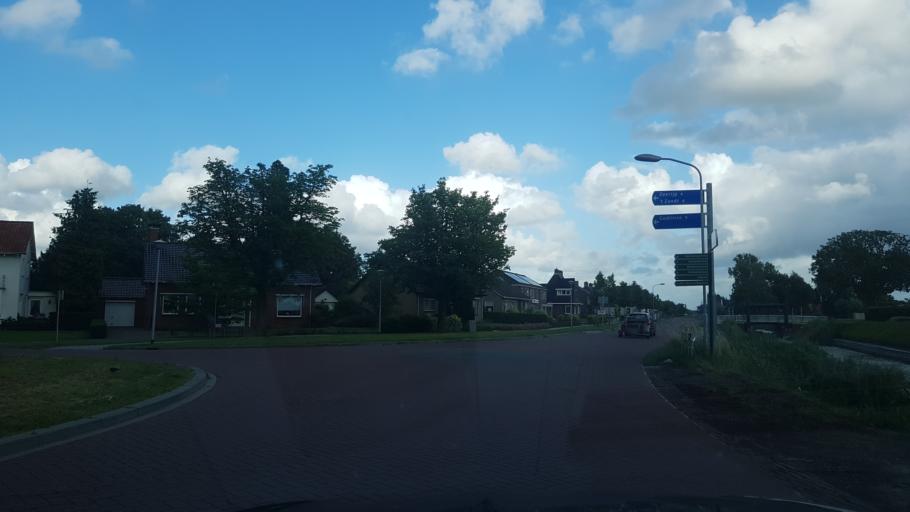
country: NL
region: Groningen
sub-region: Gemeente Appingedam
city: Appingedam
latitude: 53.3310
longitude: 6.7383
